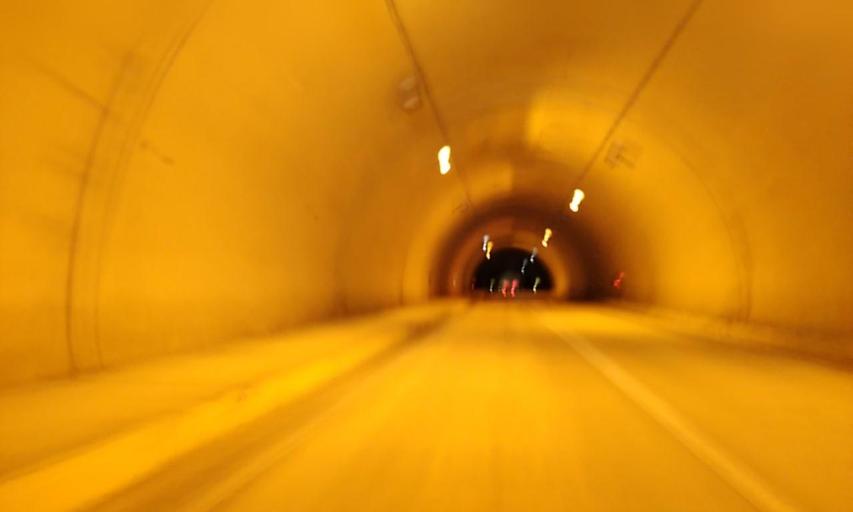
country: JP
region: Fukui
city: Obama
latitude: 35.5268
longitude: 135.8142
